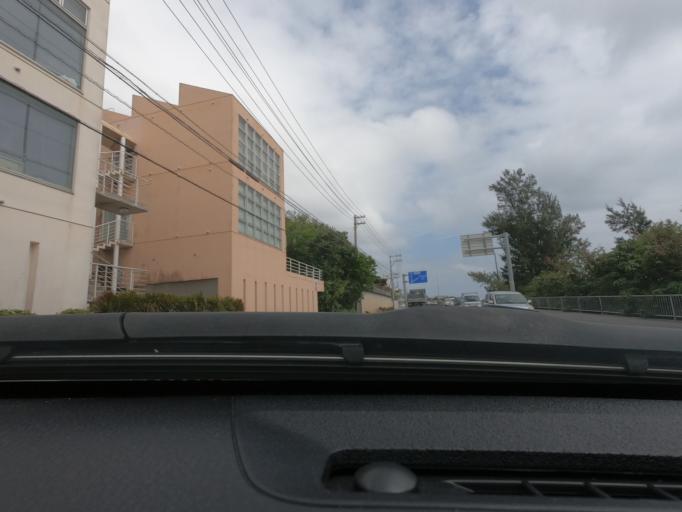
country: JP
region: Okinawa
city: Ishikawa
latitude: 26.4498
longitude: 127.9063
